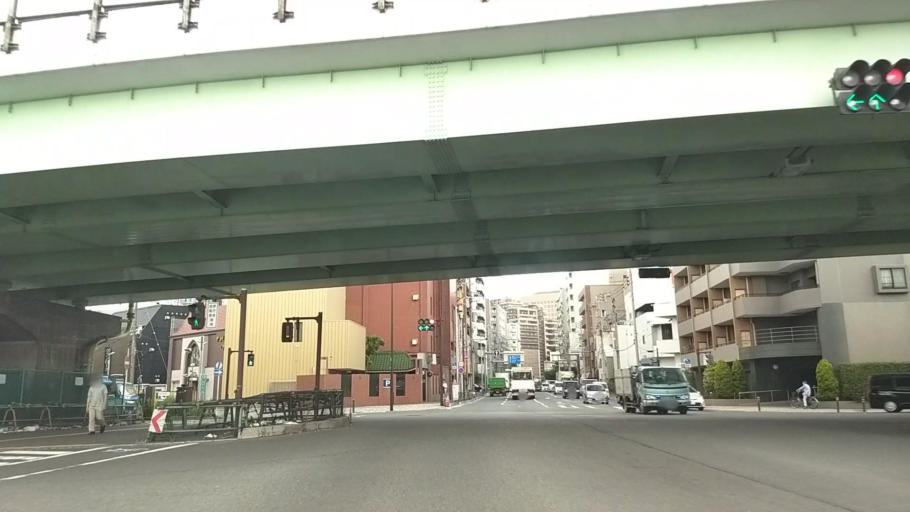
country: JP
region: Kanagawa
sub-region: Kawasaki-shi
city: Kawasaki
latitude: 35.5342
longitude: 139.7080
